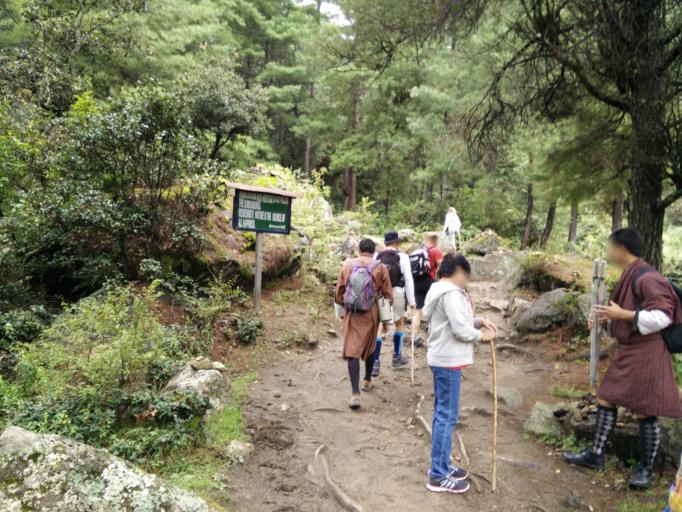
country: BT
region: Paro
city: Paro
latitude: 27.4839
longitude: 89.3613
